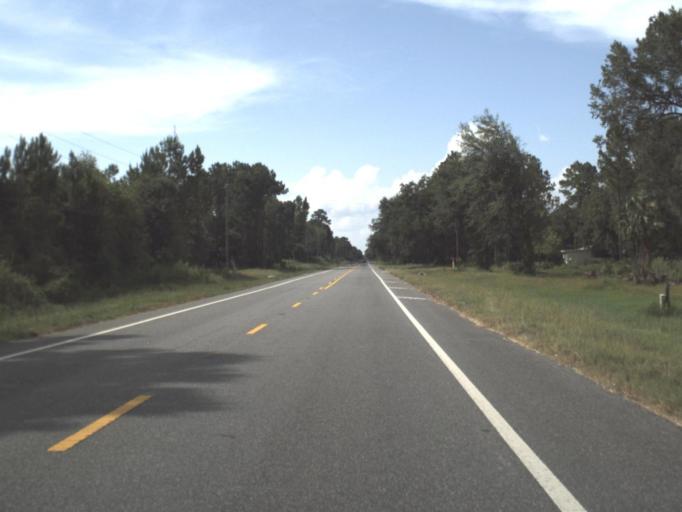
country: US
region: Florida
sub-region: Taylor County
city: Perry
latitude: 30.1822
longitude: -83.6007
